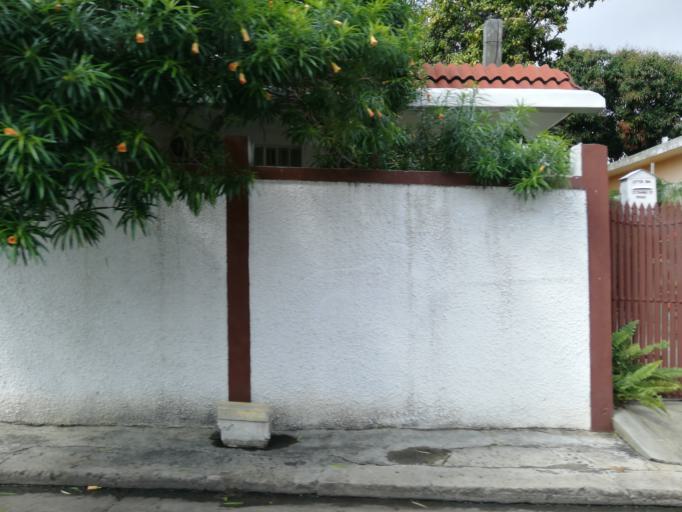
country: MU
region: Port Louis
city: Port Louis
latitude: -20.1630
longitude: 57.4824
